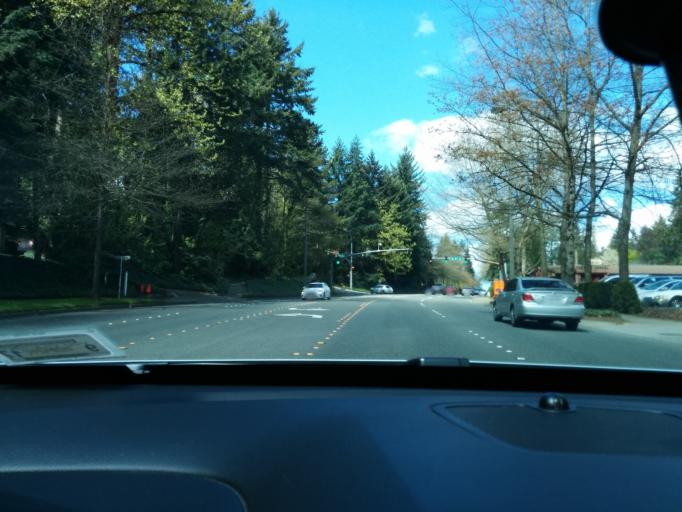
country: US
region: Washington
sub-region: King County
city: Bellevue
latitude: 47.5958
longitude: -122.1978
